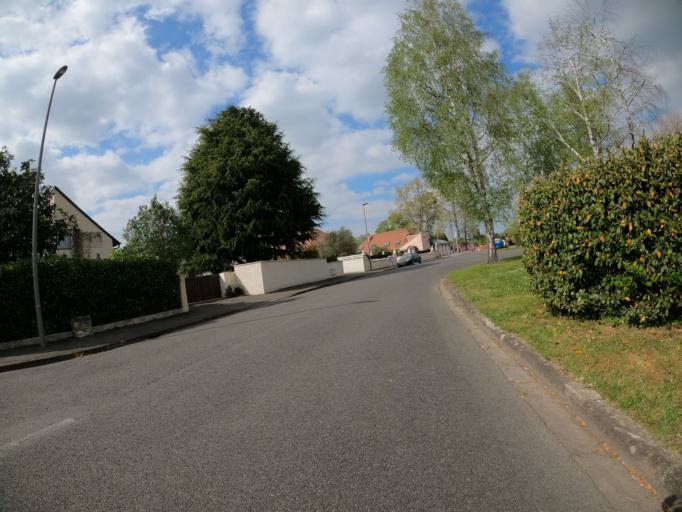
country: FR
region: Aquitaine
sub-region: Departement des Pyrenees-Atlantiques
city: Lons
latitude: 43.3258
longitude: -0.3893
